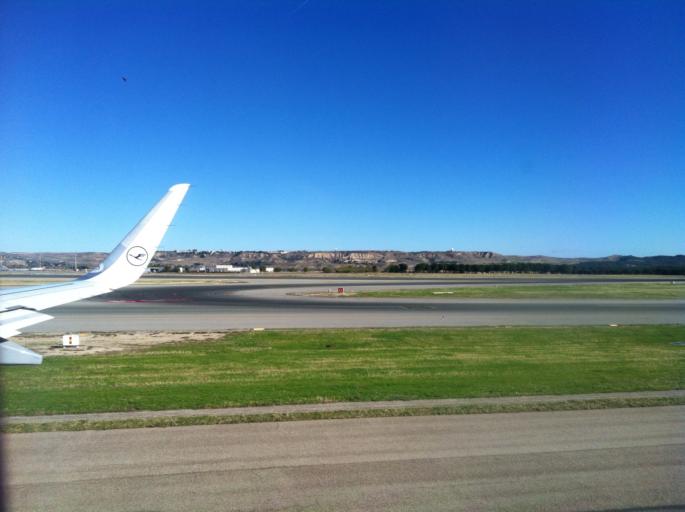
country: ES
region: Madrid
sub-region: Provincia de Madrid
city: Barajas de Madrid
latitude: 40.4809
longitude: -3.5759
